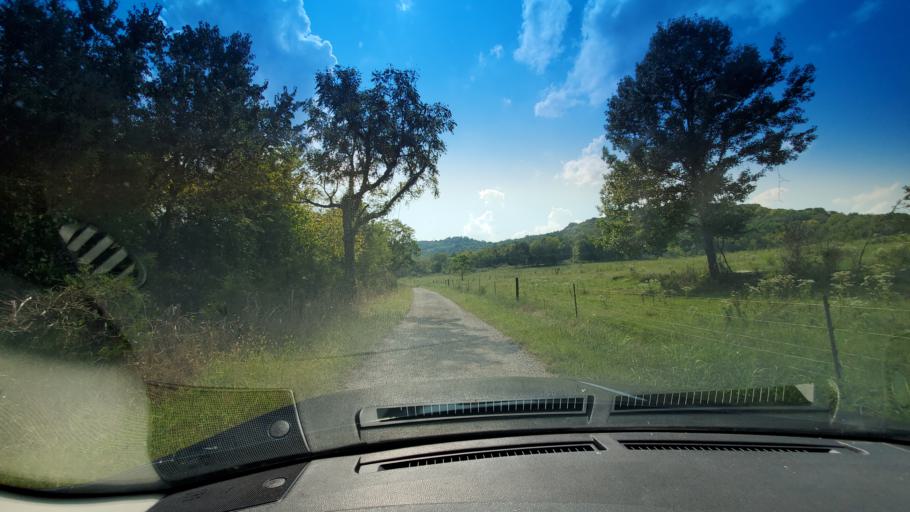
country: US
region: Tennessee
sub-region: Smith County
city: South Carthage
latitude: 36.2297
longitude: -85.9888
